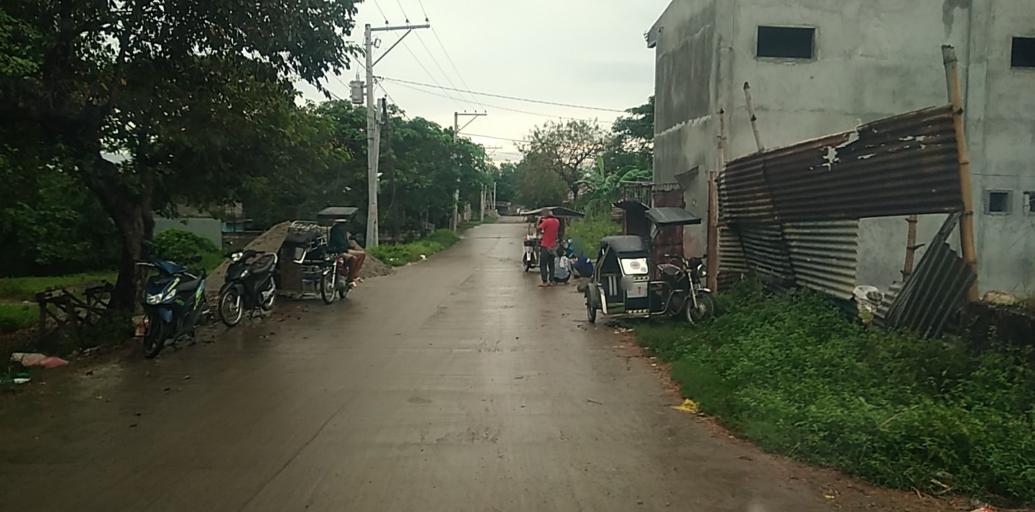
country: PH
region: Central Luzon
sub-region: Province of Pampanga
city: Arayat
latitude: 15.1515
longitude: 120.7480
